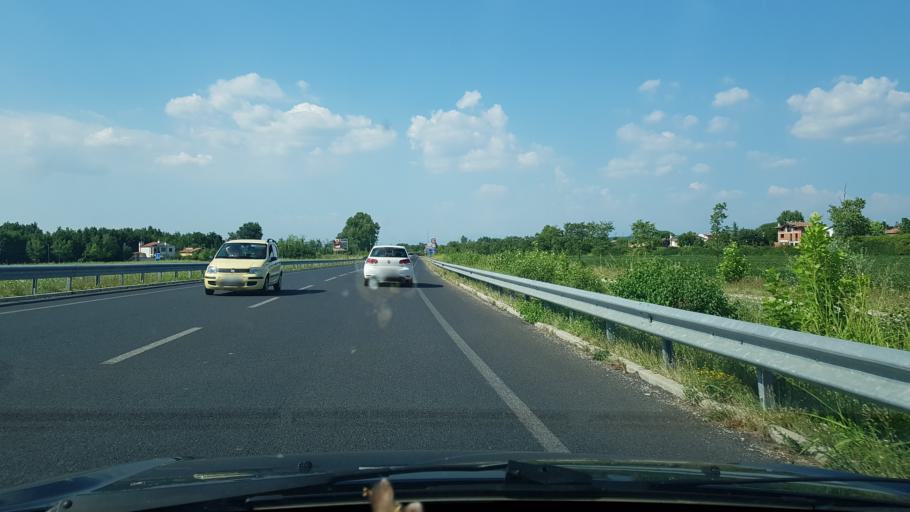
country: IT
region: Friuli Venezia Giulia
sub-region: Provincia di Gorizia
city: Staranzano
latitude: 45.8021
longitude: 13.4883
